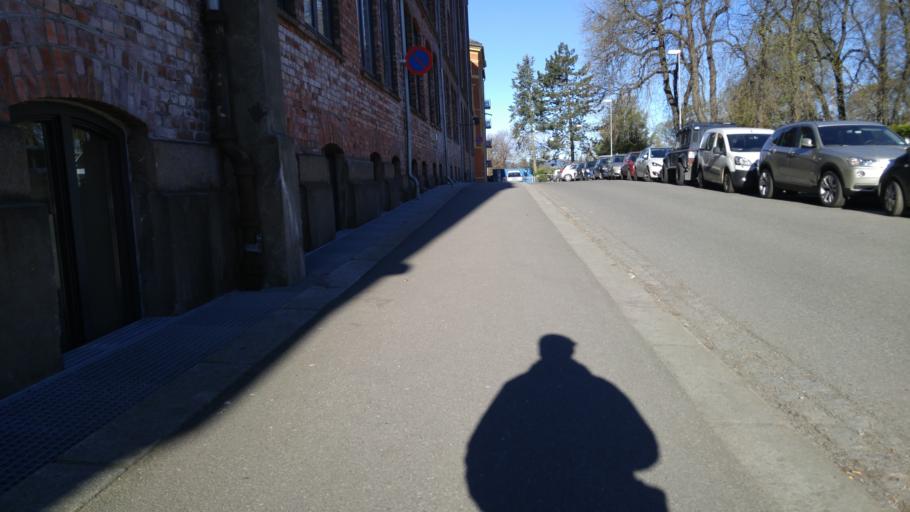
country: NO
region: Oslo
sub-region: Oslo
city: Oslo
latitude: 59.9032
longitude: 10.7733
